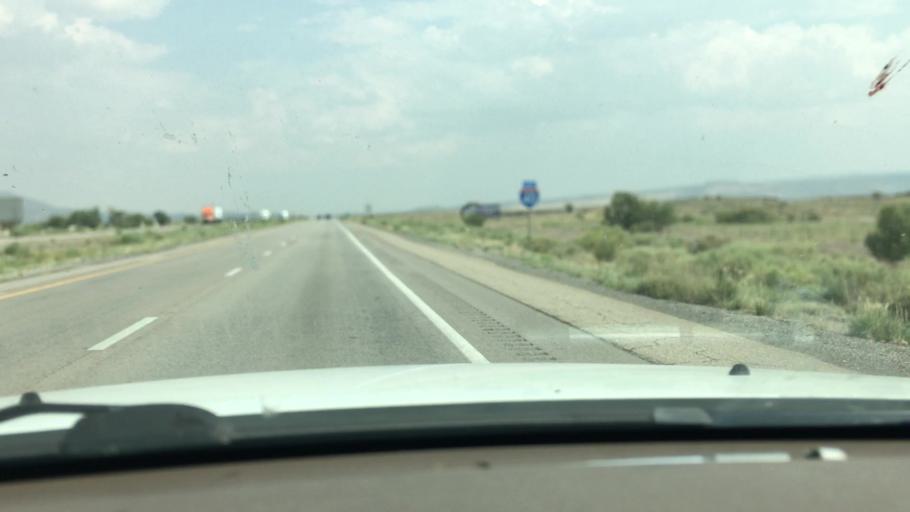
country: US
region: New Mexico
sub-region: Cibola County
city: Grants
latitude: 35.1188
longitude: -107.8218
